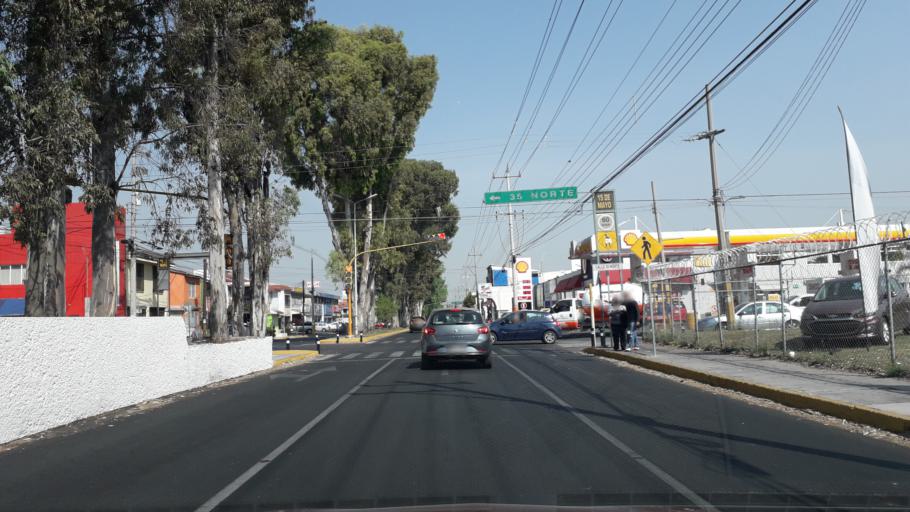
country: MX
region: Puebla
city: Puebla
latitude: 19.0667
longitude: -98.2163
